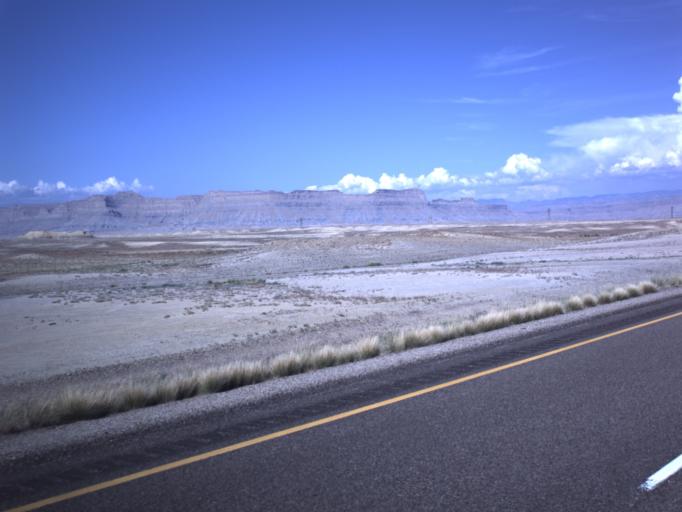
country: US
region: Utah
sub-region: Carbon County
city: East Carbon City
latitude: 38.9600
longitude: -110.2906
